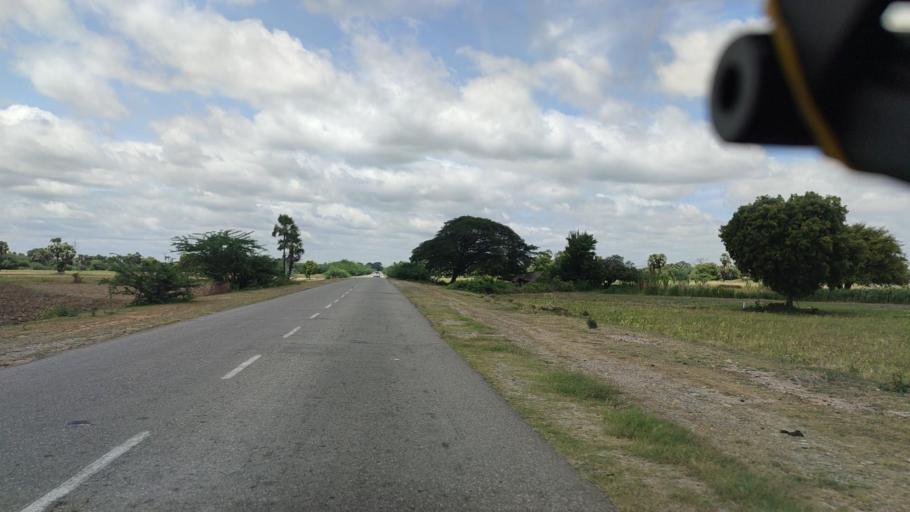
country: MM
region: Mandalay
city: Meiktila
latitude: 20.8422
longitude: 95.9436
